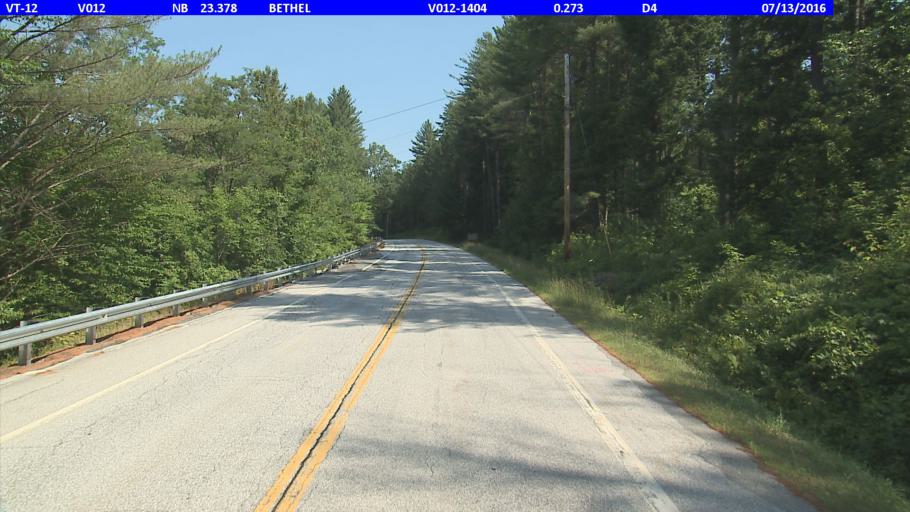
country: US
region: Vermont
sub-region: Orange County
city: Randolph
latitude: 43.7947
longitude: -72.6495
